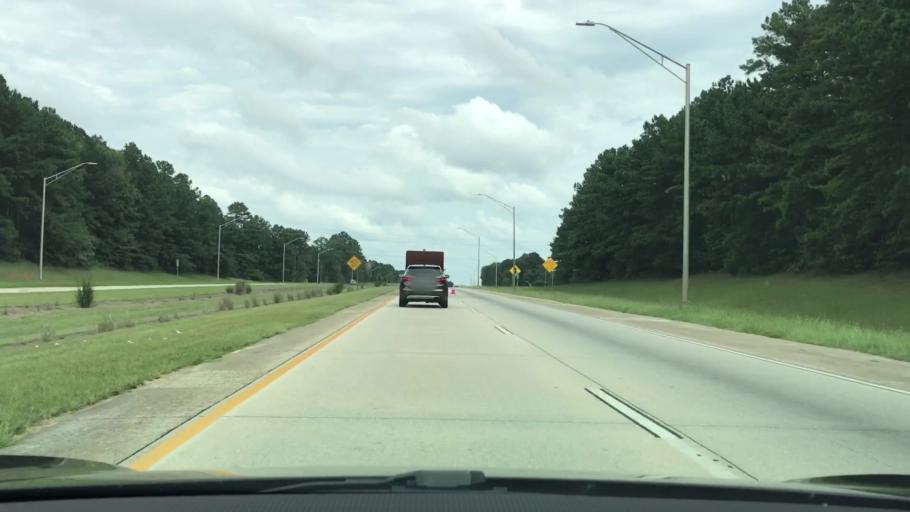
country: US
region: Georgia
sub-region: Troup County
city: La Grange
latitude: 33.0396
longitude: -84.9715
